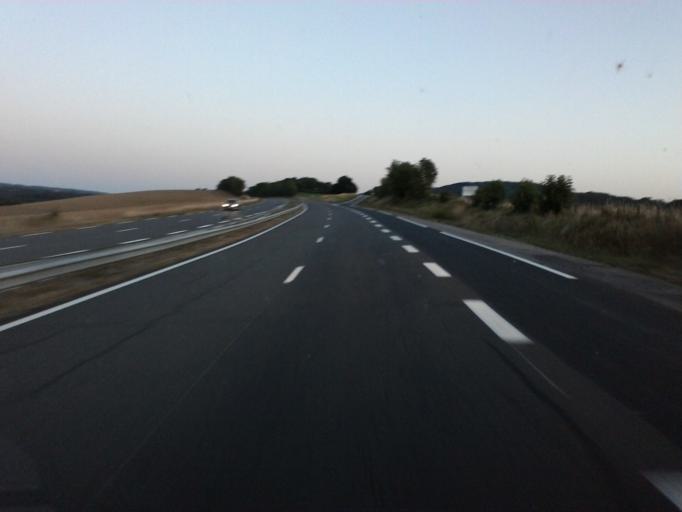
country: FR
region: Franche-Comte
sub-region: Departement du Jura
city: Montmorot
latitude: 46.7423
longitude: 5.5554
